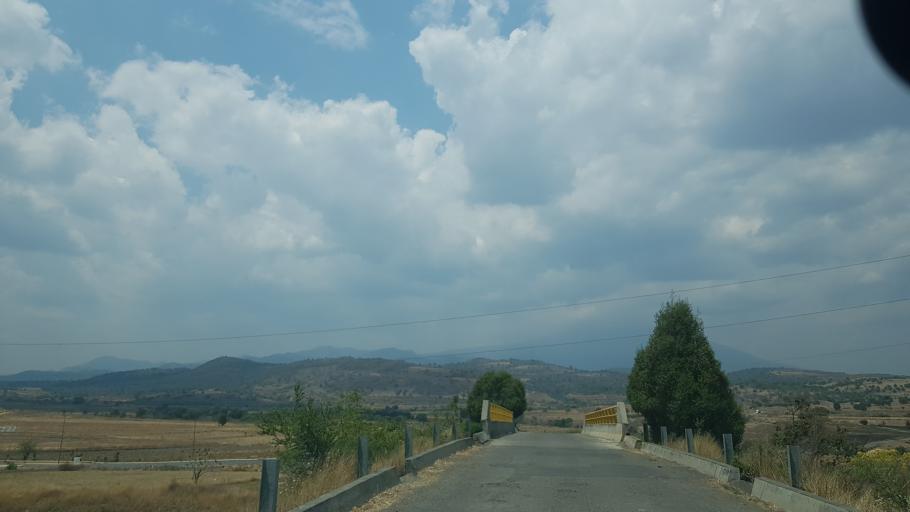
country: MX
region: Puebla
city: San Juan Amecac
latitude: 18.8196
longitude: -98.6235
